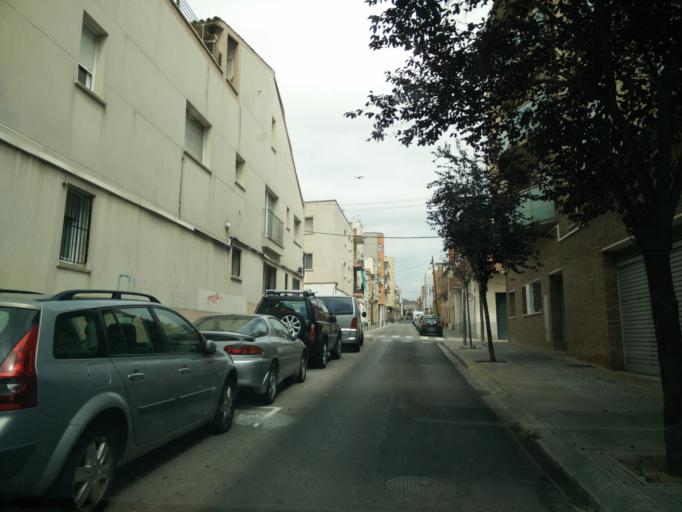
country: ES
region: Catalonia
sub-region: Provincia de Barcelona
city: Terrassa
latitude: 41.5713
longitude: 2.0147
